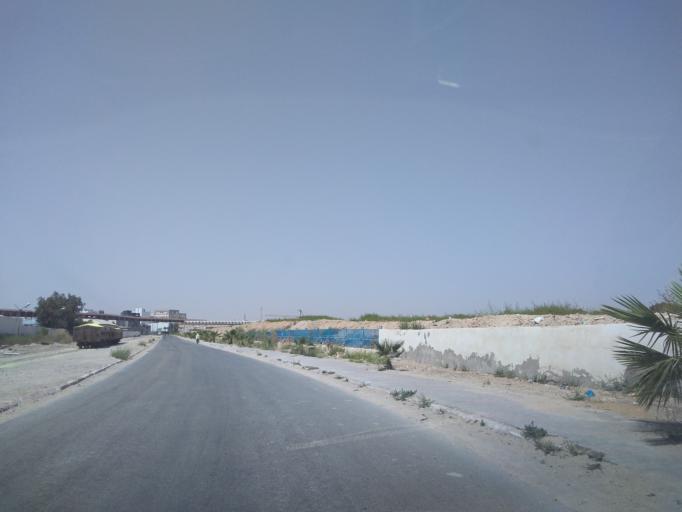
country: TN
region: Safaqis
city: Sfax
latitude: 34.7321
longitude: 10.7759
